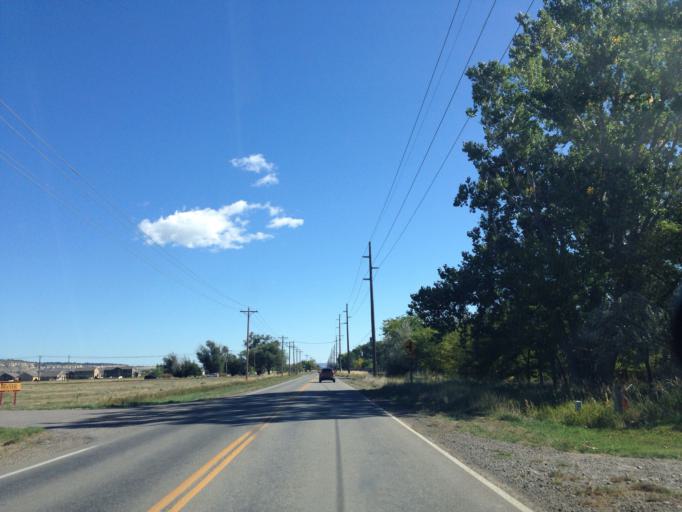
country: US
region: Montana
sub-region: Yellowstone County
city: Billings
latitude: 45.7841
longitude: -108.6559
